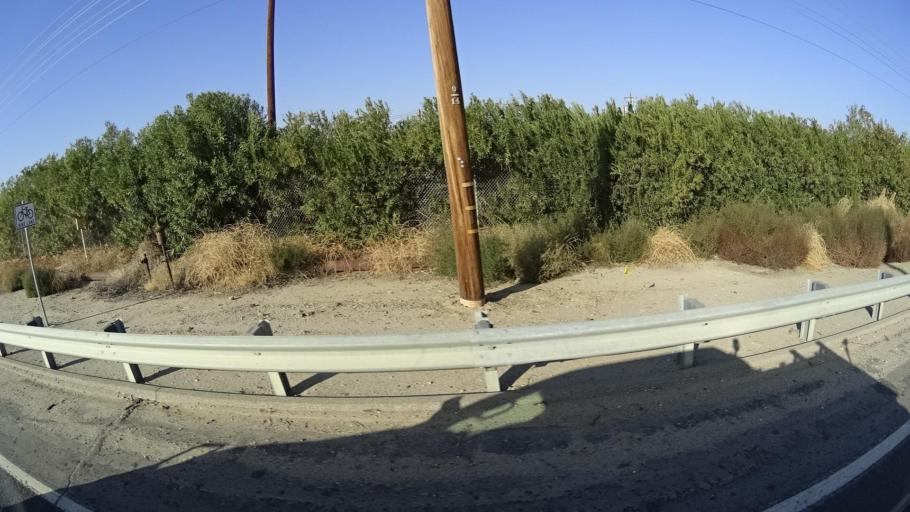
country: US
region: California
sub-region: Kern County
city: Oildale
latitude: 35.4269
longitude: -118.9988
